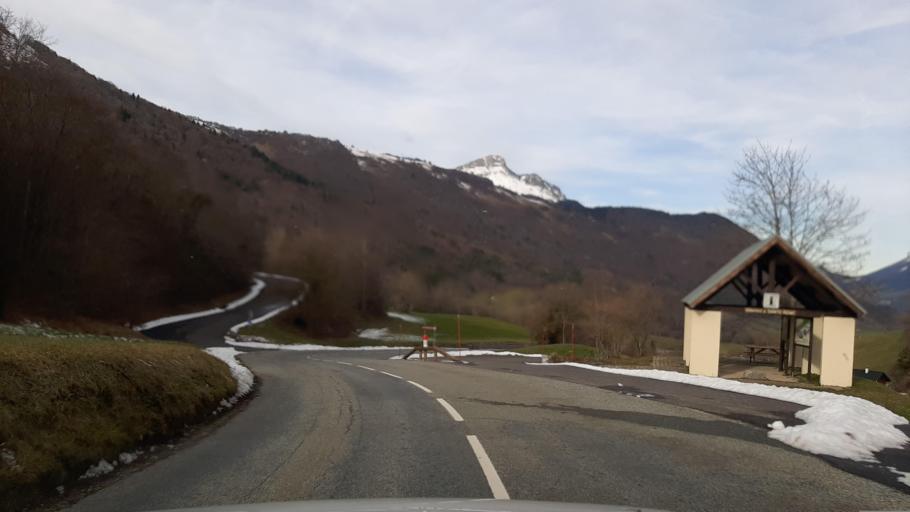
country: FR
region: Rhone-Alpes
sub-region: Departement de la Savoie
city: Coise-Saint-Jean-Pied-Gauthier
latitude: 45.5902
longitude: 6.1379
